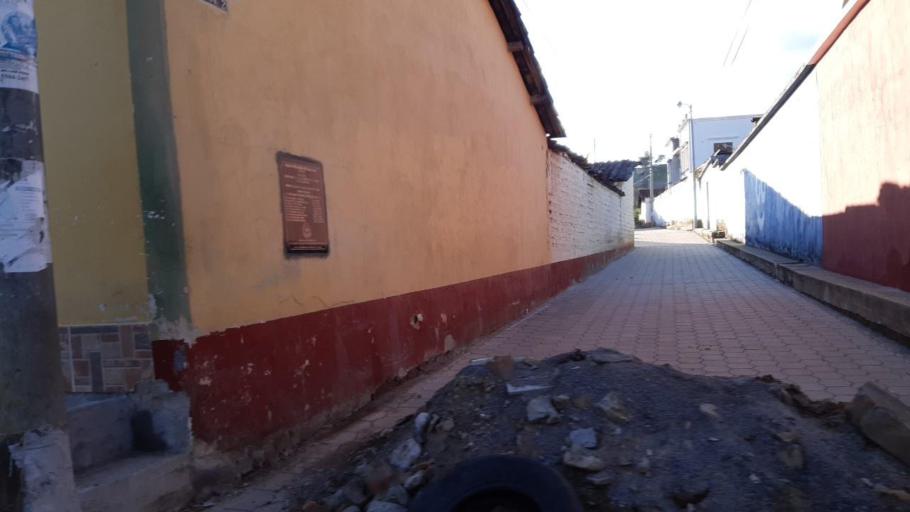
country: GT
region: Quetzaltenango
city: Salcaja
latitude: 14.8795
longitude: -91.4608
